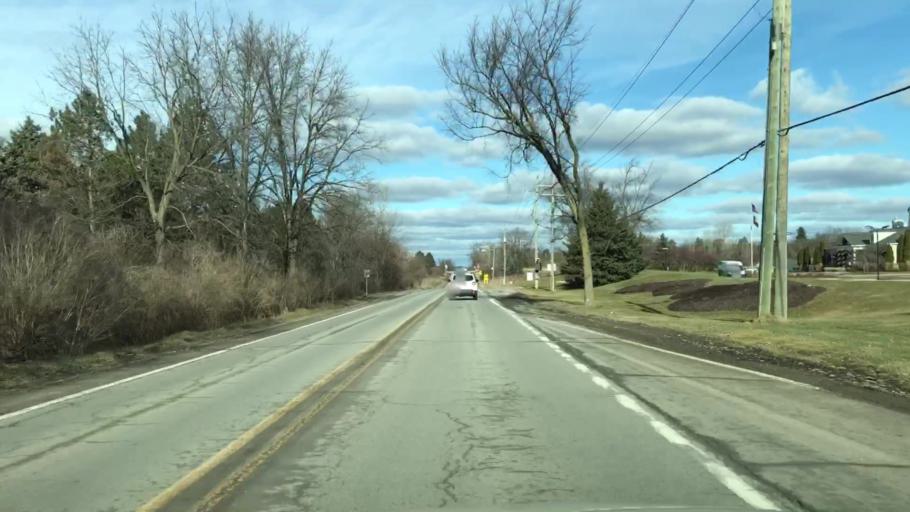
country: US
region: Michigan
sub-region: Oakland County
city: Auburn Hills
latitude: 42.7350
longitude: -83.1967
